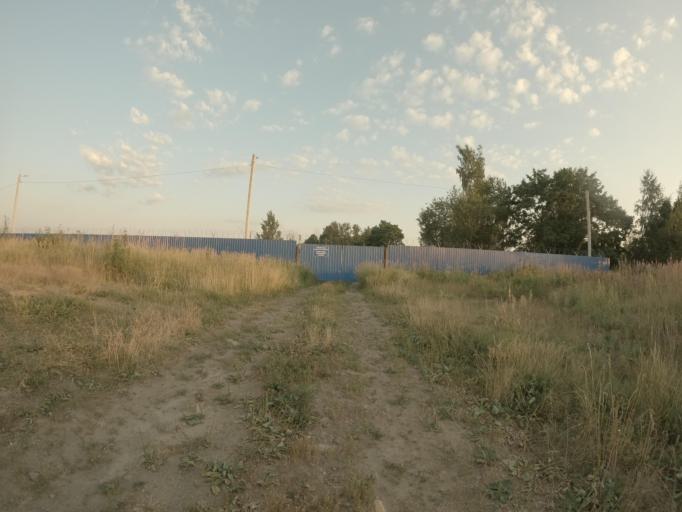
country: RU
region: Leningrad
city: Pavlovo
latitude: 59.8472
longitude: 30.9422
